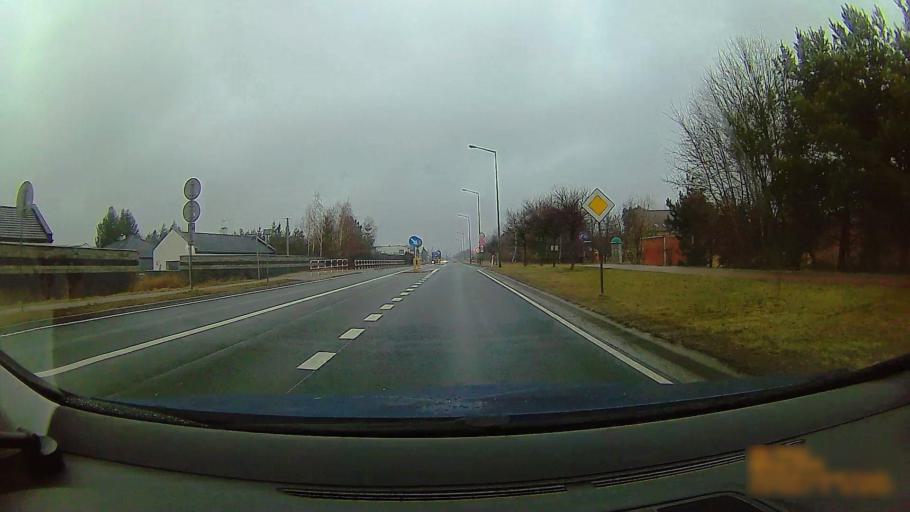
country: PL
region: Greater Poland Voivodeship
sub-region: Konin
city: Konin
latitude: 52.1785
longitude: 18.2708
